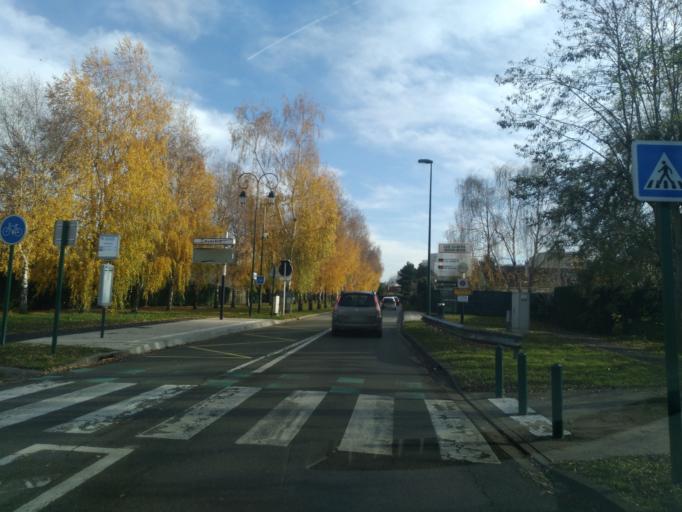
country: FR
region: Ile-de-France
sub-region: Departement des Yvelines
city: Plaisir
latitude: 48.8217
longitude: 1.9663
